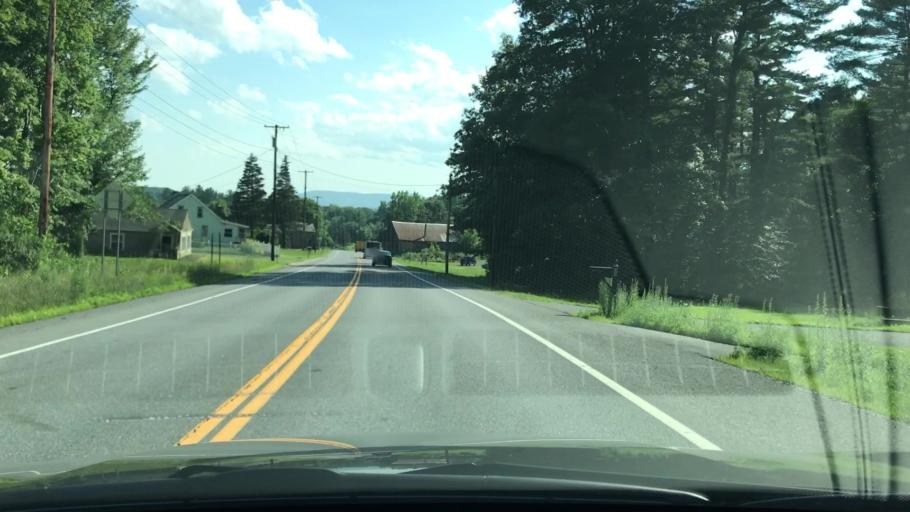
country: US
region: New York
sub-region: Warren County
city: Queensbury
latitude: 43.3812
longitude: -73.6579
